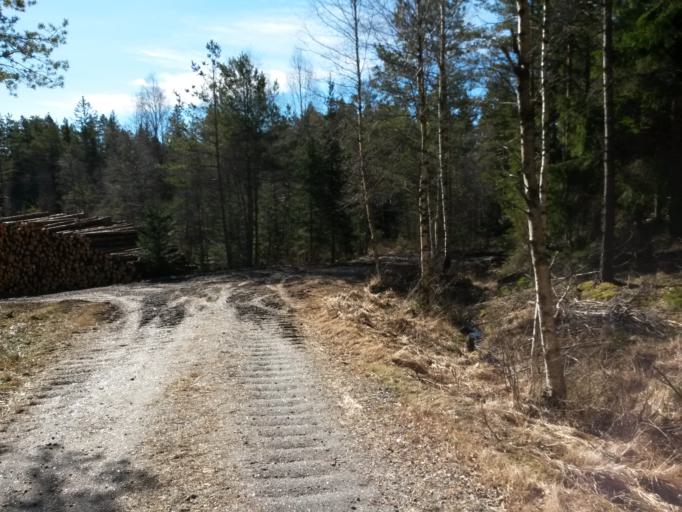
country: SE
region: Vaestra Goetaland
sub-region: Vargarda Kommun
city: Jonstorp
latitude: 57.9611
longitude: 12.6809
